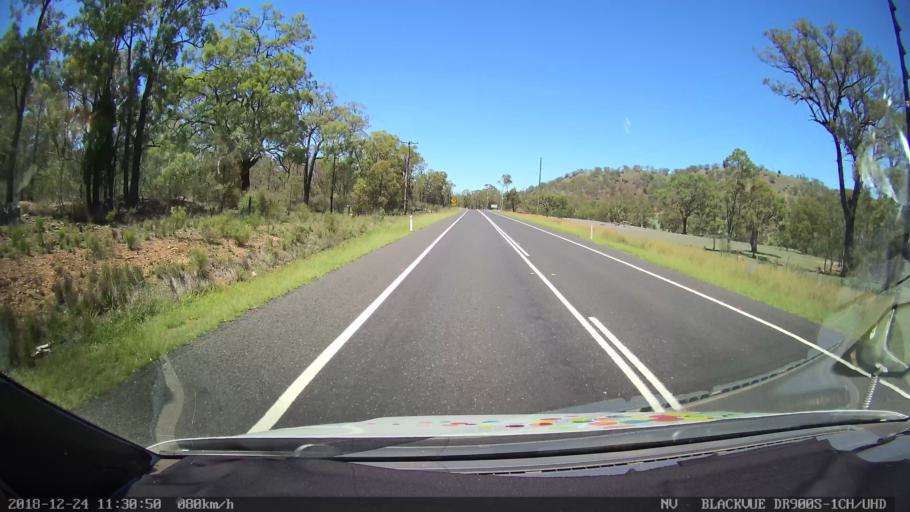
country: AU
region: New South Wales
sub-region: Upper Hunter Shire
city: Merriwa
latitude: -32.2089
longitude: 150.4632
